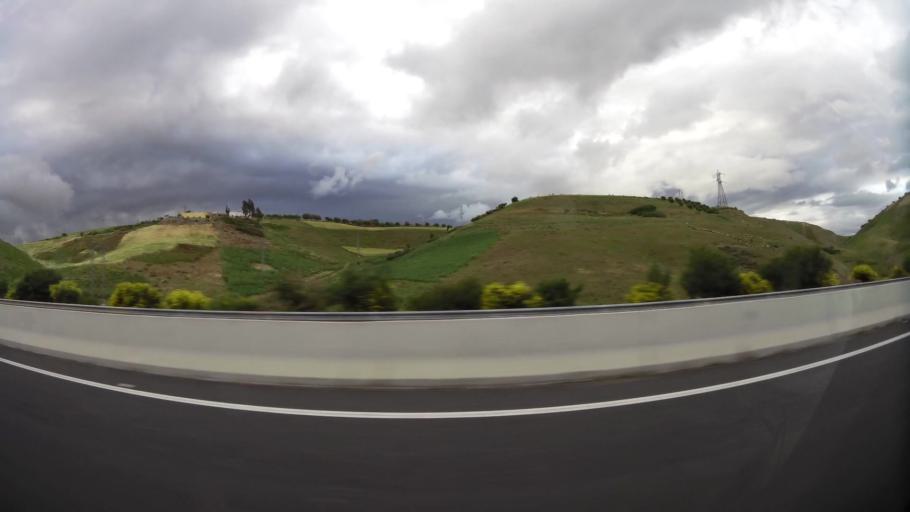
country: MA
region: Taza-Al Hoceima-Taounate
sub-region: Taza
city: Taza
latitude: 34.2606
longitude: -3.9462
